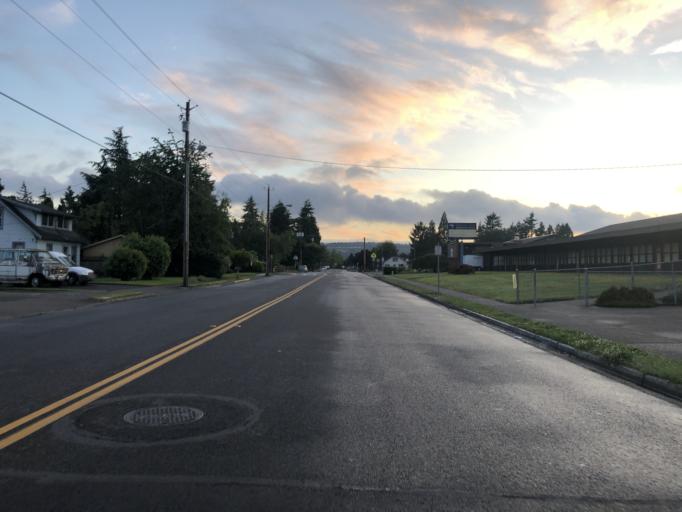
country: US
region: Washington
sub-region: King County
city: Auburn
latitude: 47.3203
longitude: -122.2146
